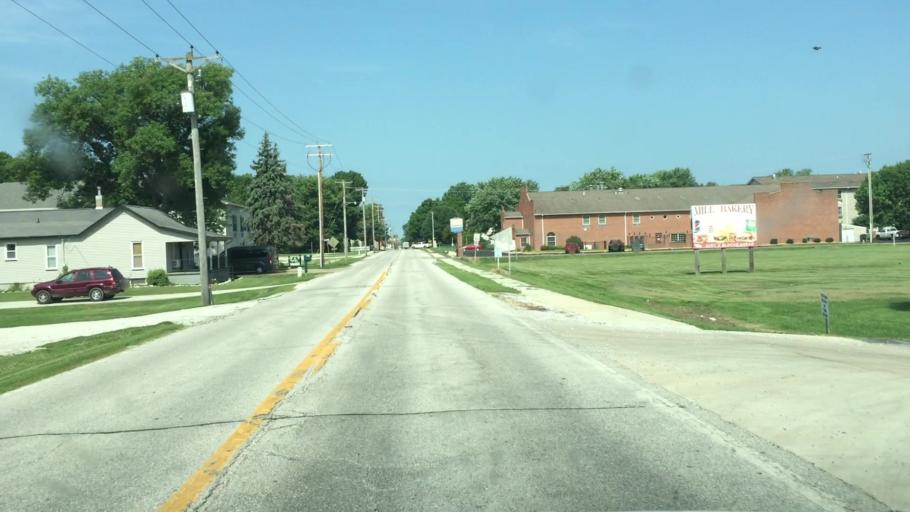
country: US
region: Illinois
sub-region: Hancock County
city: Nauvoo
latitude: 40.5496
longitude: -91.3708
